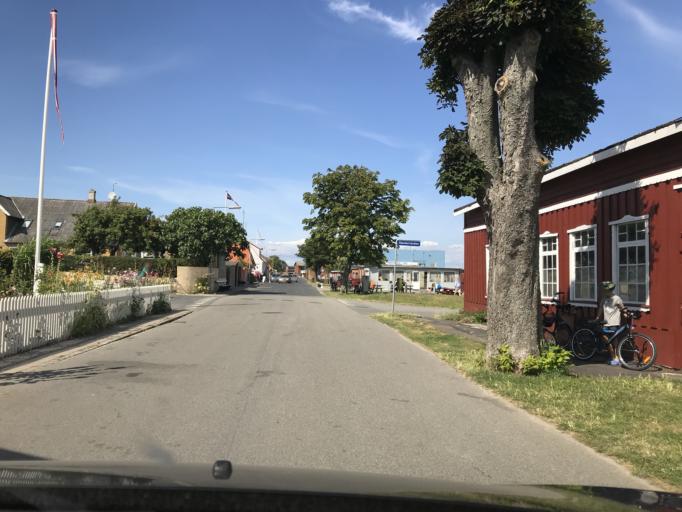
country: DK
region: South Denmark
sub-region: AEro Kommune
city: Marstal
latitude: 54.8507
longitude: 10.5215
